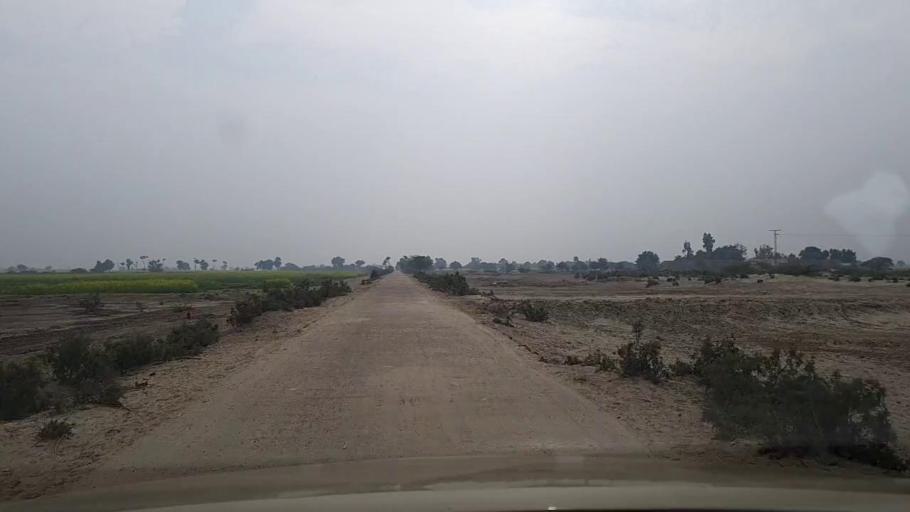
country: PK
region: Sindh
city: Sanghar
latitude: 26.1181
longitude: 68.9043
